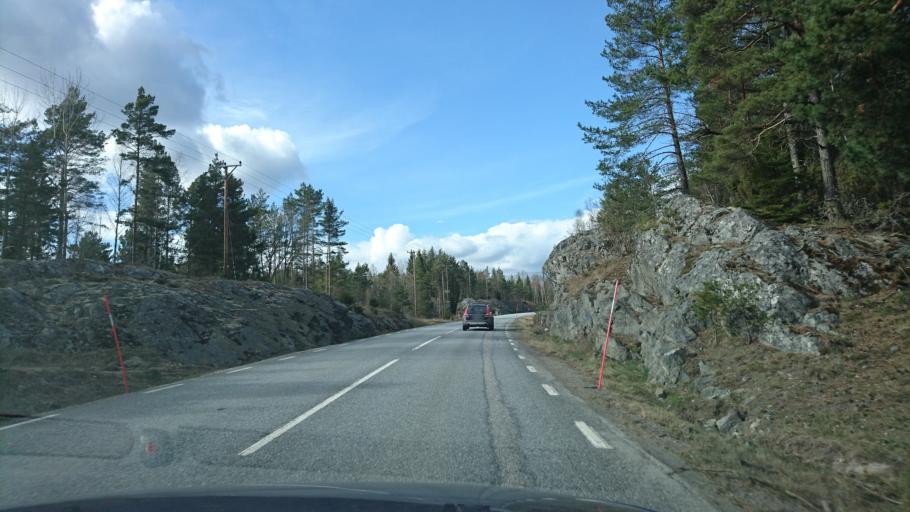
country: SE
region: Stockholm
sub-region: Nynashamns Kommun
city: Nynashamn
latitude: 58.9534
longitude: 17.9984
